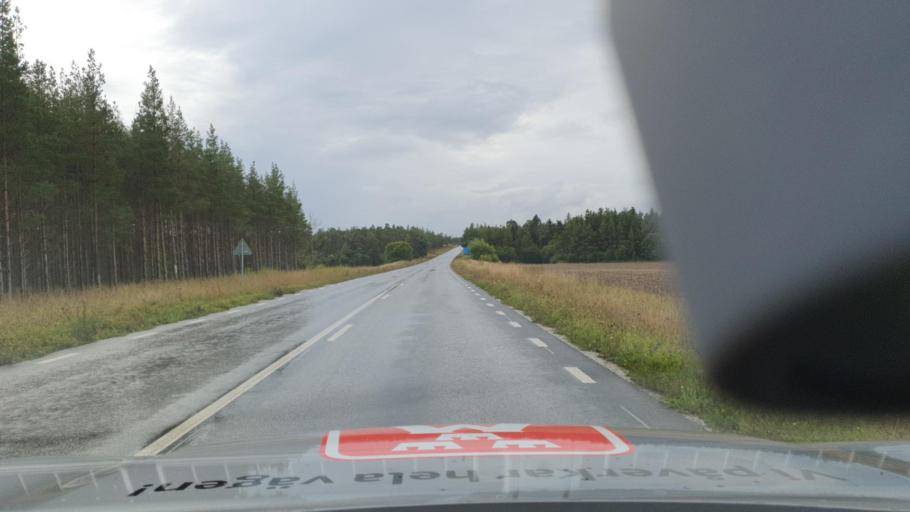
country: SE
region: Gotland
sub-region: Gotland
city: Slite
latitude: 57.7566
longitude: 18.7905
